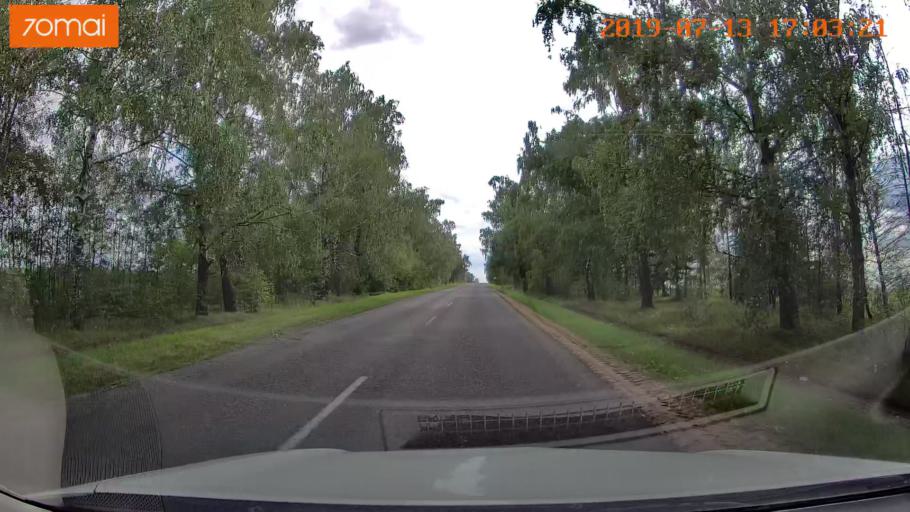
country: BY
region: Mogilev
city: Kirawsk
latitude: 53.2769
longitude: 29.3780
